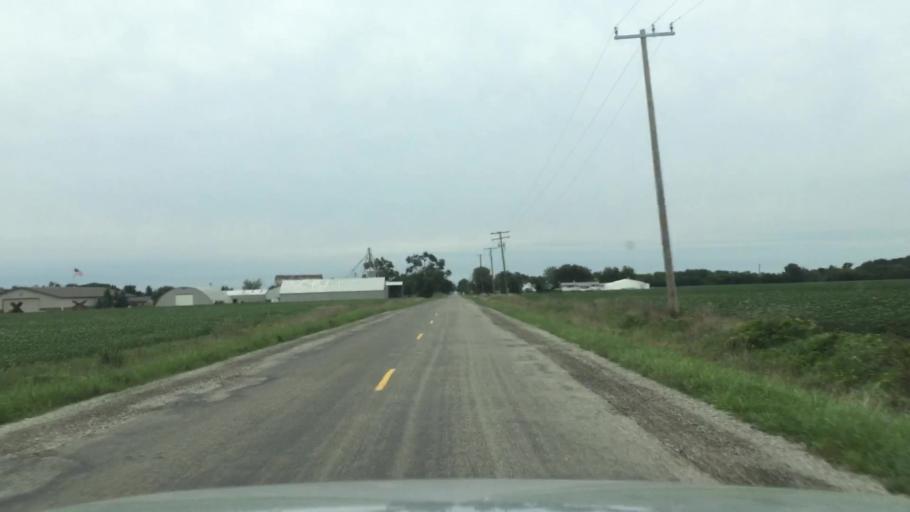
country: US
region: Michigan
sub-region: Washtenaw County
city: Milan
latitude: 42.0797
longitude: -83.7358
